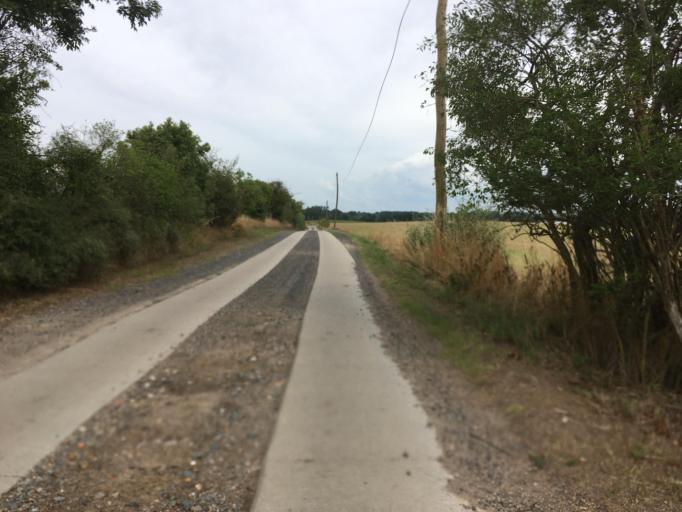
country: DE
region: Brandenburg
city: Gerswalde
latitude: 53.1979
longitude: 13.8300
